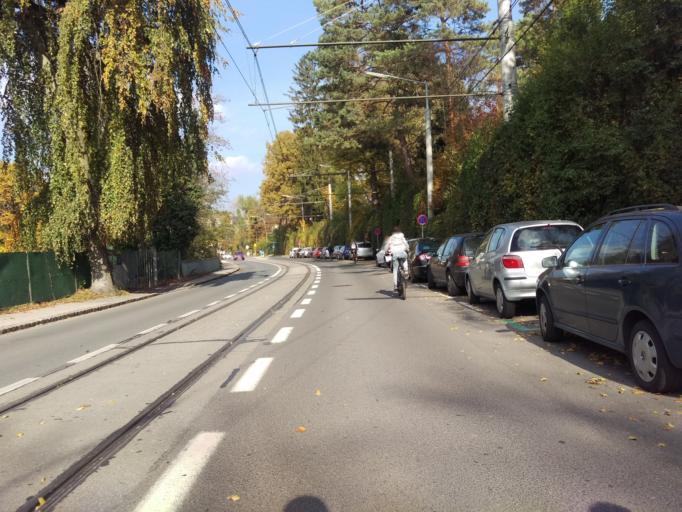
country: AT
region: Styria
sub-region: Graz Stadt
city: Graz
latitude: 47.0852
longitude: 15.4604
